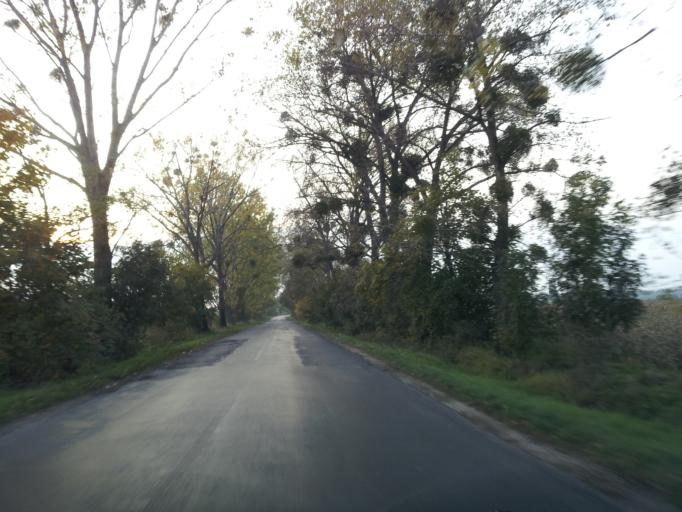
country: HU
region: Komarom-Esztergom
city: Kisber
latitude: 47.4713
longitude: 17.9349
